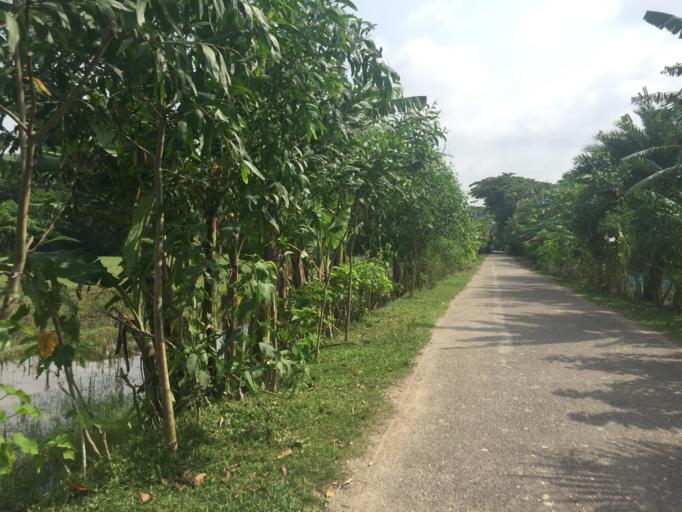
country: BD
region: Barisal
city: Mathba
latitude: 22.2586
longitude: 89.9110
